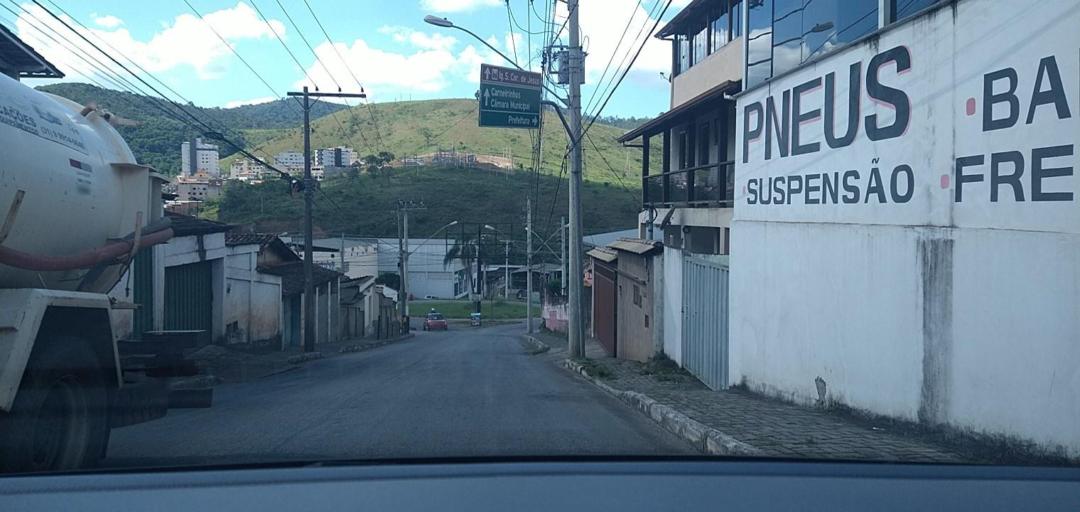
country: BR
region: Minas Gerais
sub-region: Joao Monlevade
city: Joao Monlevade
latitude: -19.8130
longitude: -43.1929
